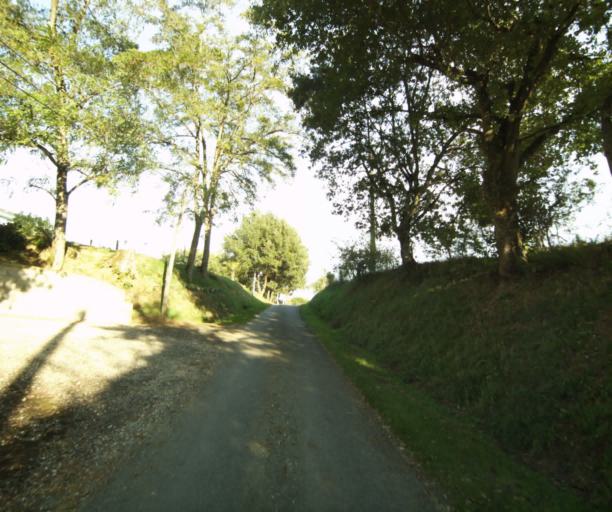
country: FR
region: Midi-Pyrenees
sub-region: Departement du Gers
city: Cazaubon
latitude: 43.8617
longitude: -0.0014
